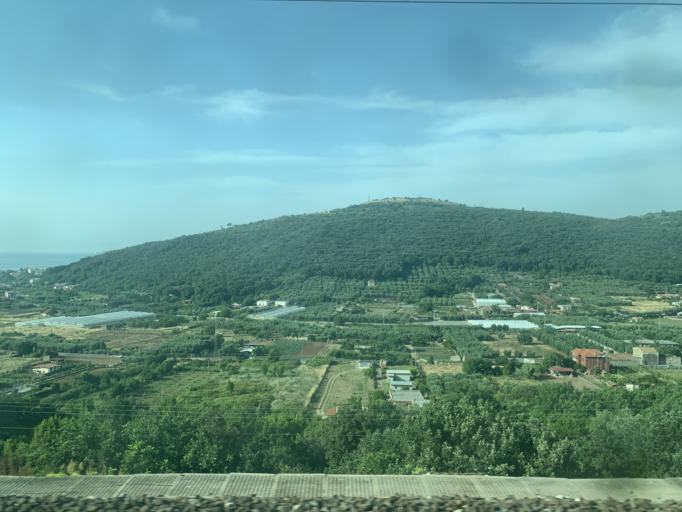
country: IT
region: Latium
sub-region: Provincia di Latina
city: Gaeta
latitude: 41.2558
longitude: 13.5712
